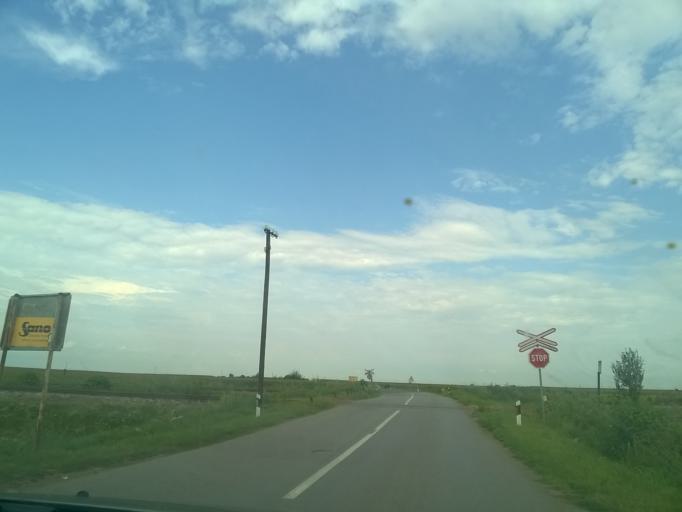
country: RS
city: Orlovat
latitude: 45.2502
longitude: 20.5763
